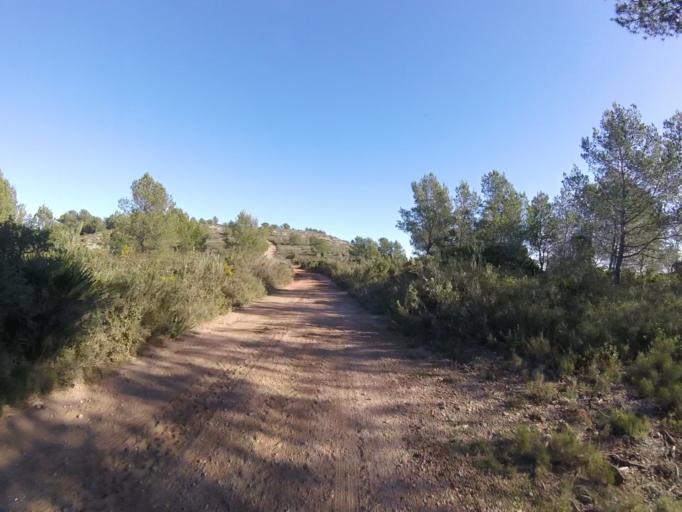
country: ES
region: Valencia
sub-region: Provincia de Castello
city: Orpesa/Oropesa del Mar
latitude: 40.0968
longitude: 0.1067
